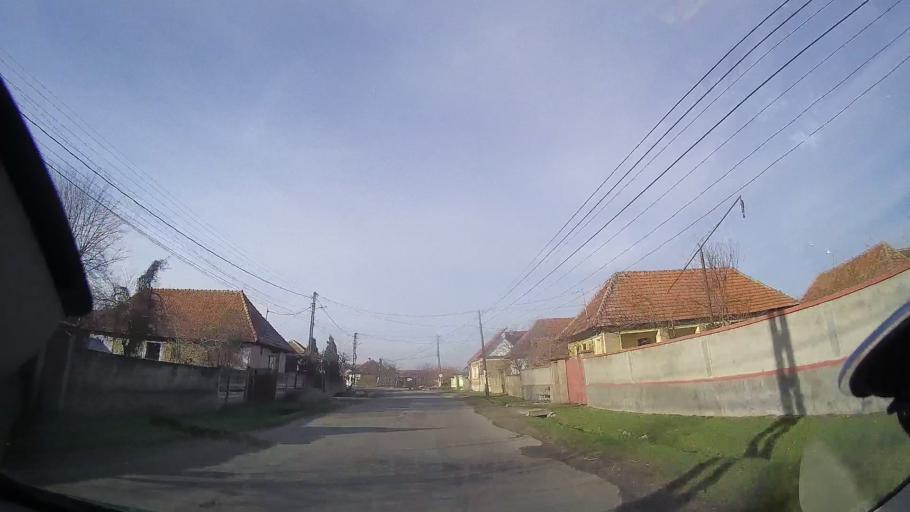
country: RO
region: Bihor
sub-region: Comuna Brusturi
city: Brusturi
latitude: 47.1535
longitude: 22.2457
